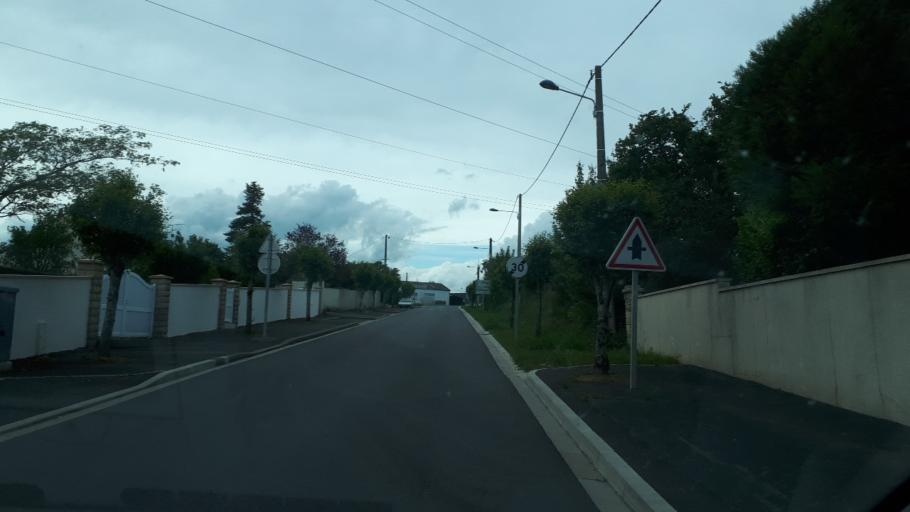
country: FR
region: Centre
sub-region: Departement de l'Indre
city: Reuilly
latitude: 47.0882
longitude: 2.0357
